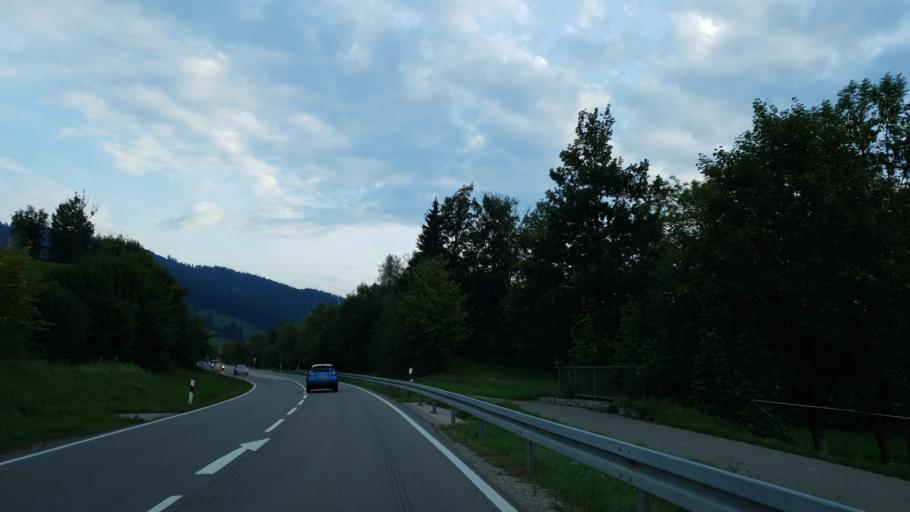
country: DE
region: Bavaria
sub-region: Swabia
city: Weitnau
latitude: 47.6672
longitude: 10.0949
